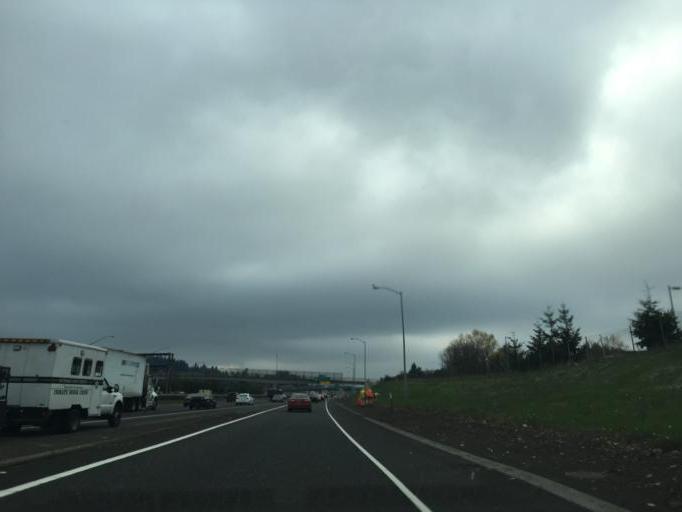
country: US
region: Oregon
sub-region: Multnomah County
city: Lents
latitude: 45.5164
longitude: -122.5658
